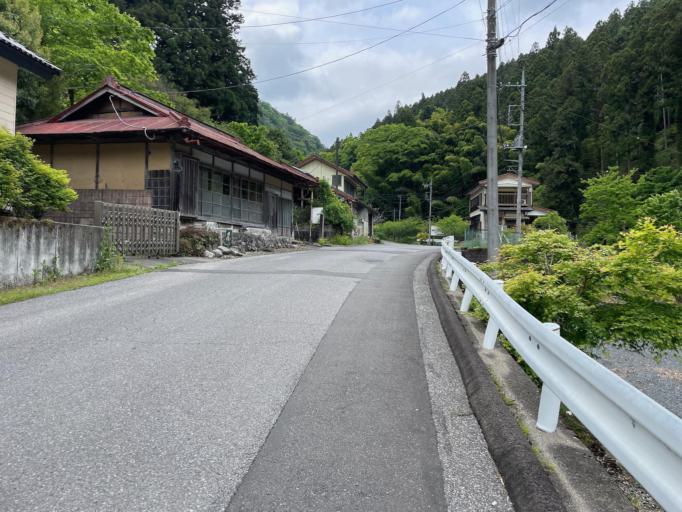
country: JP
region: Tochigi
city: Tanuma
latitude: 36.4735
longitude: 139.5938
